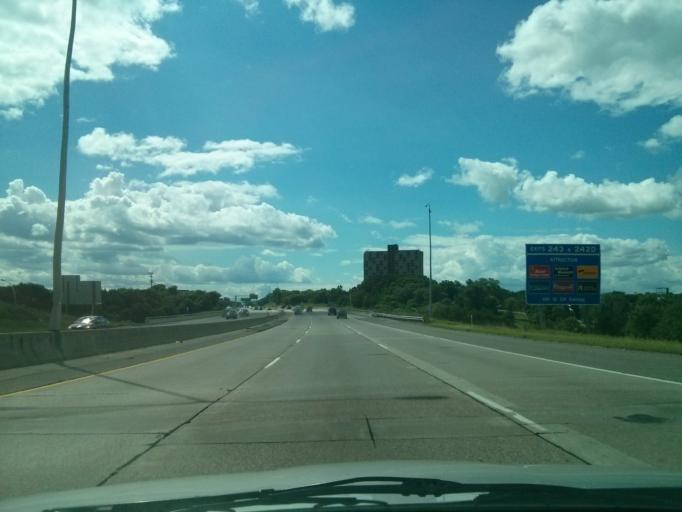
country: US
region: Minnesota
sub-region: Ramsey County
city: Maplewood
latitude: 44.9527
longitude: -93.0385
